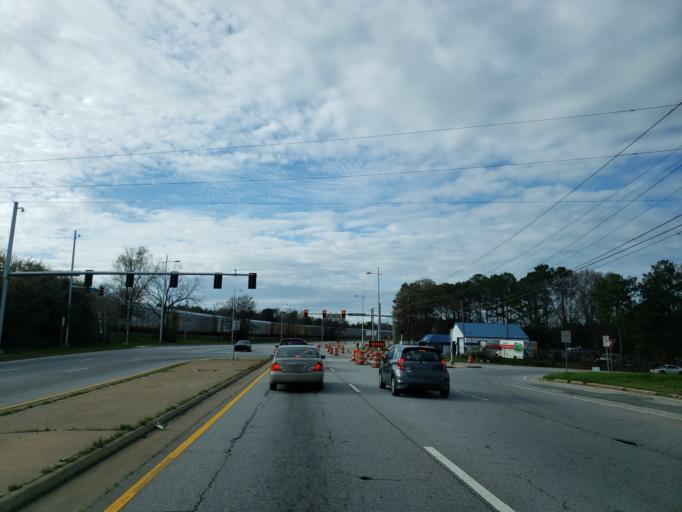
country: US
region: Georgia
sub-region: Clayton County
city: Forest Park
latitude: 33.6327
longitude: -84.3885
